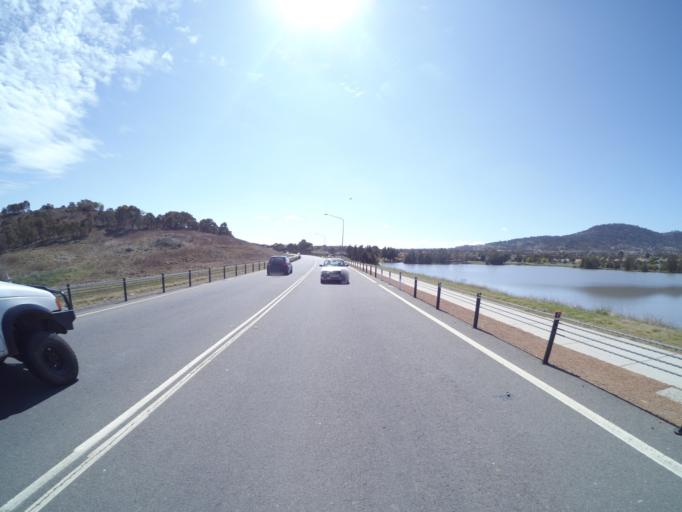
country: AU
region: Australian Capital Territory
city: Macarthur
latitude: -35.4545
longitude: 149.0798
